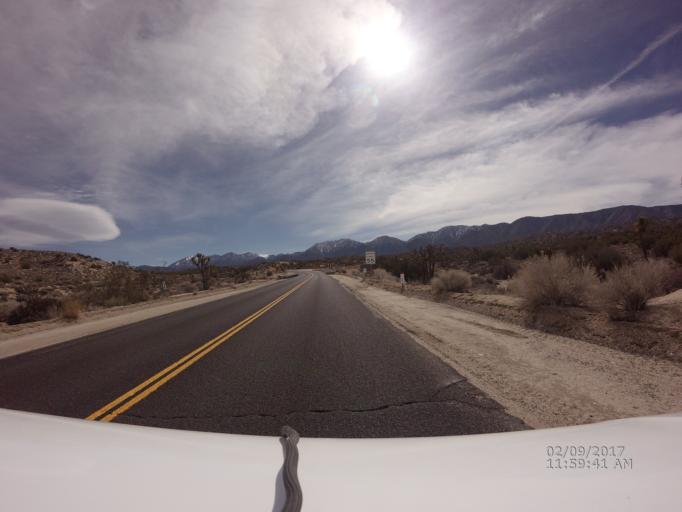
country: US
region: California
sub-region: Los Angeles County
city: Littlerock
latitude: 34.4731
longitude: -117.8998
